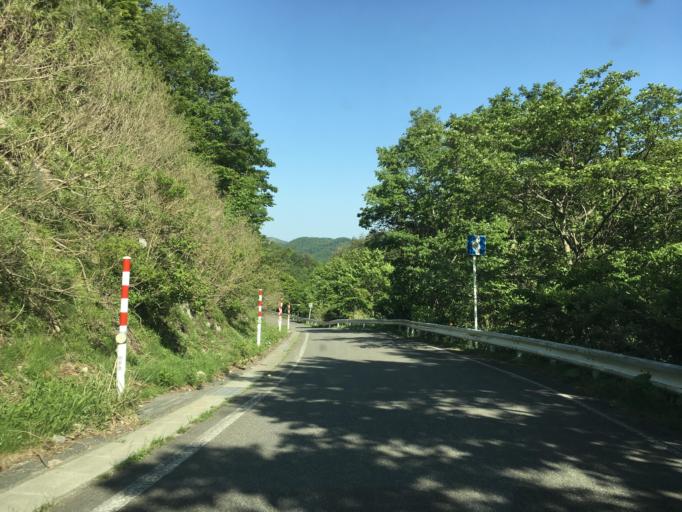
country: JP
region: Iwate
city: Ofunato
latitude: 39.1855
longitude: 141.7461
